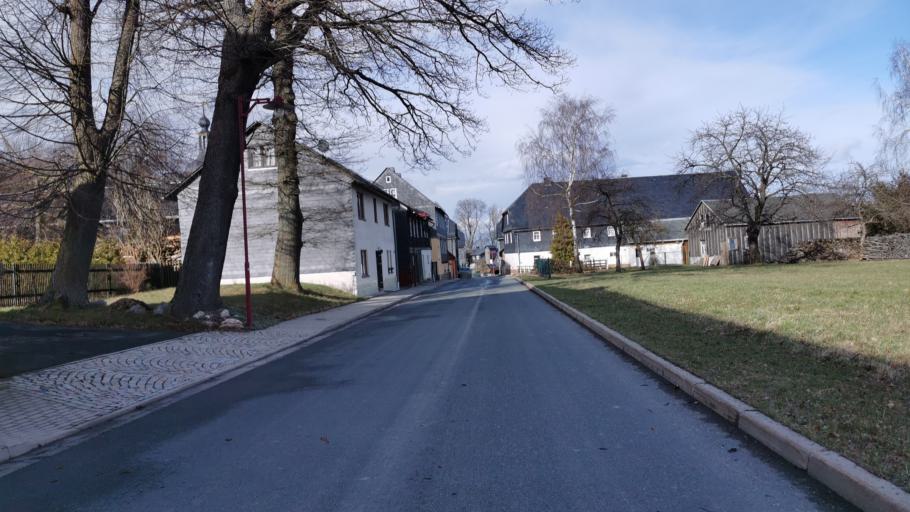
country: DE
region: Thuringia
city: Leutenberg
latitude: 50.5142
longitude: 11.4521
